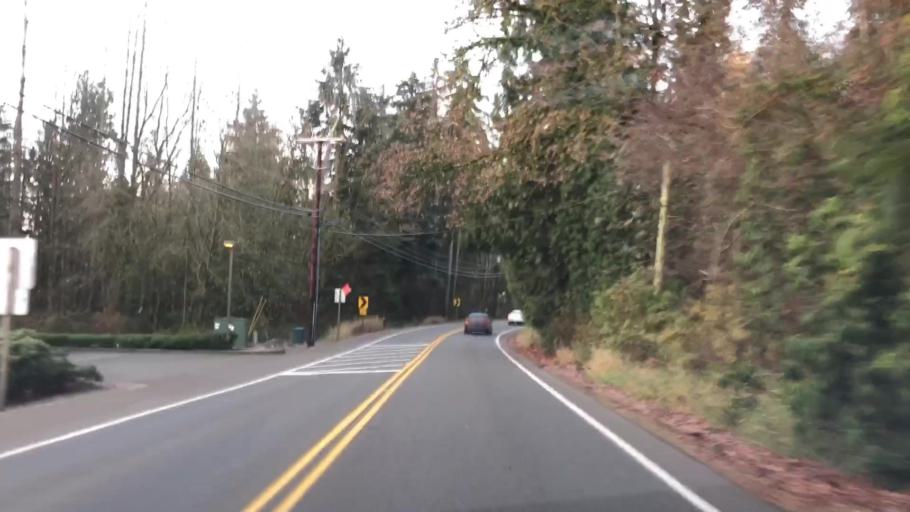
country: US
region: Washington
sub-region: King County
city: Cottage Lake
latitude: 47.7181
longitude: -122.0818
